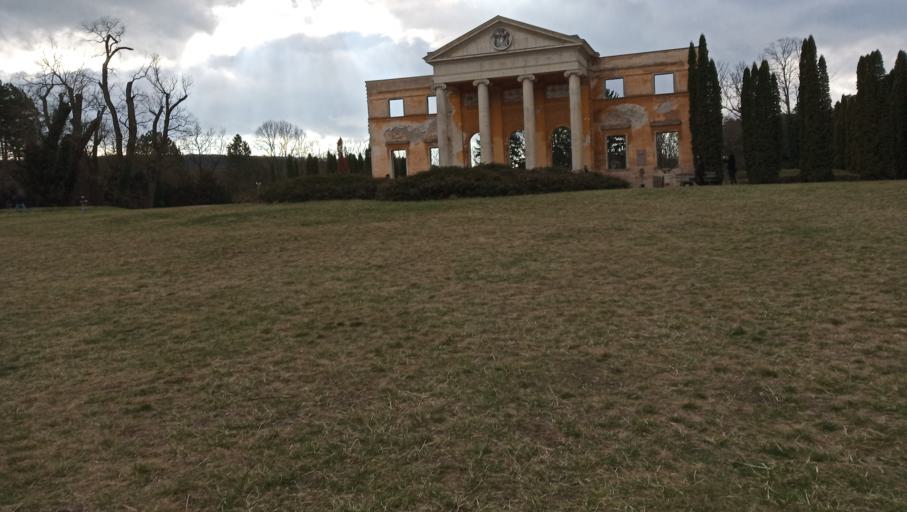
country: HU
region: Fejer
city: Bicske
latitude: 47.4237
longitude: 18.5908
